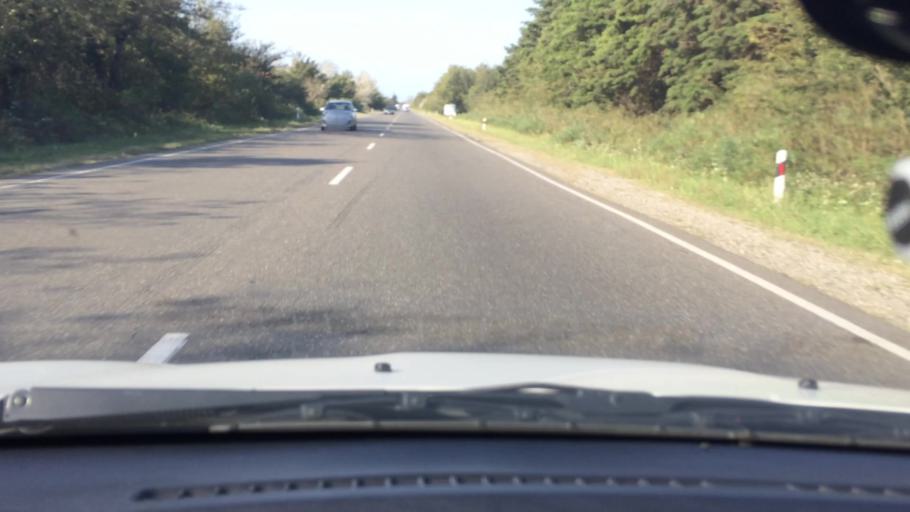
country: GE
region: Imereti
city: Vani
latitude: 42.1965
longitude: 42.5164
